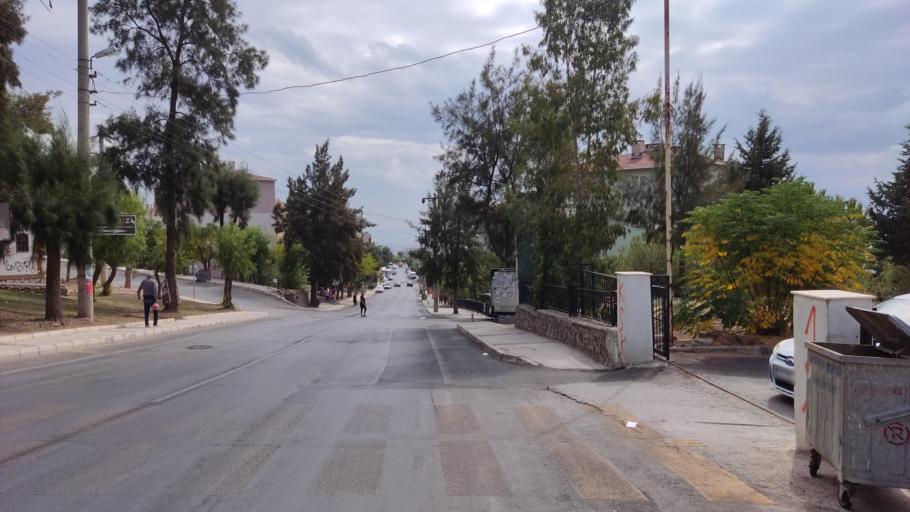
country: TR
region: Izmir
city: Karsiyaka
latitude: 38.4991
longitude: 27.0876
